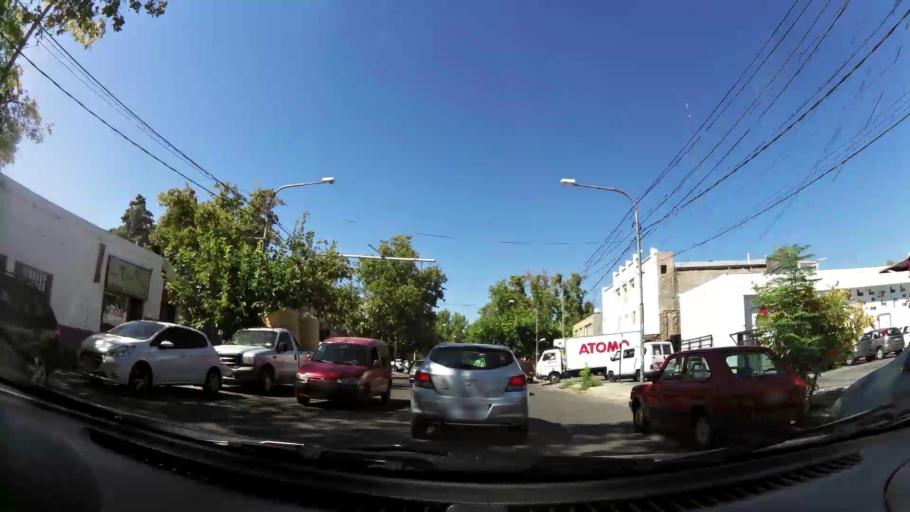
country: AR
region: Mendoza
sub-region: Departamento de Godoy Cruz
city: Godoy Cruz
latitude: -32.9095
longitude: -68.8605
